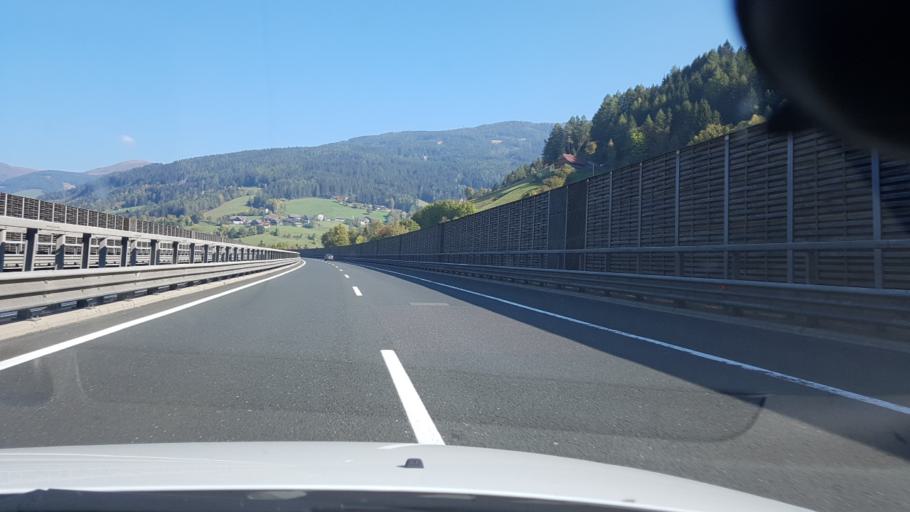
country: AT
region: Carinthia
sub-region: Politischer Bezirk Spittal an der Drau
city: Gmuend
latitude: 46.9315
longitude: 13.5997
